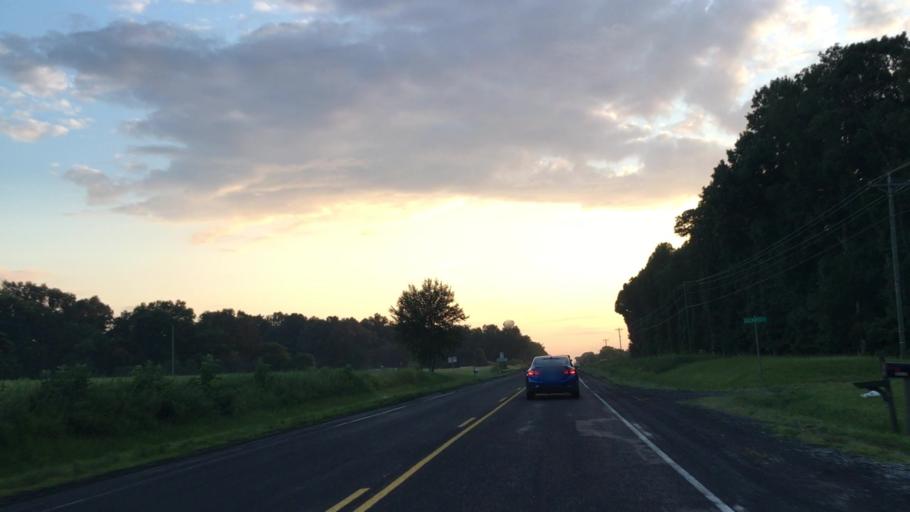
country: US
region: Virginia
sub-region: Spotsylvania County
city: Spotsylvania
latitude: 38.3103
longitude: -77.7866
